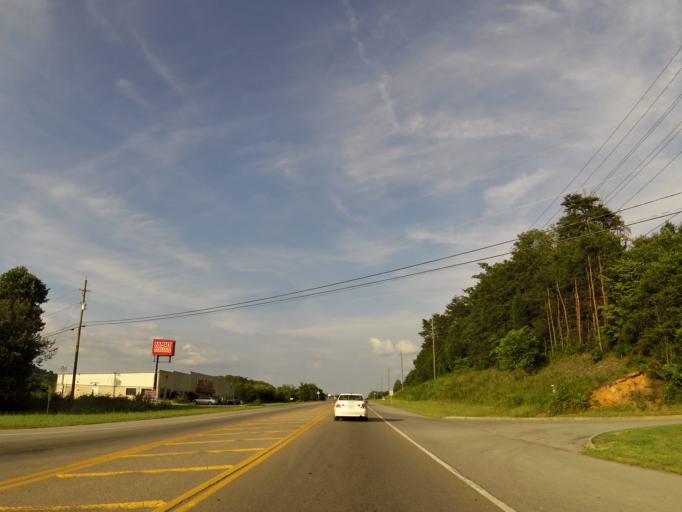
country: US
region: Tennessee
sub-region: Sevier County
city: Sevierville
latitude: 35.8710
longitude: -83.4968
